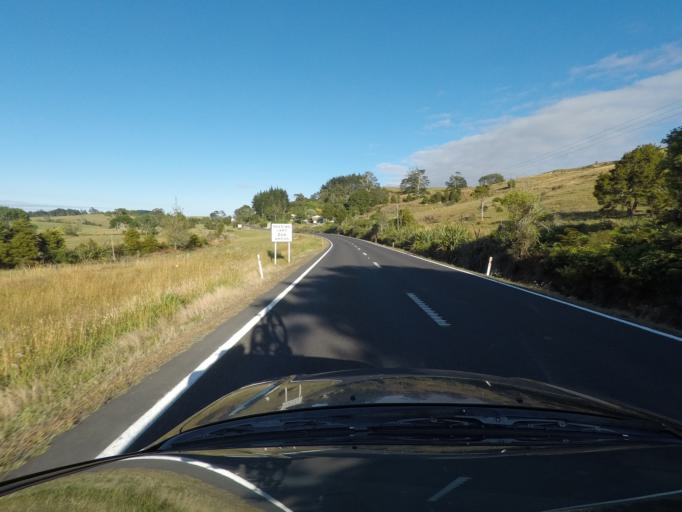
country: NZ
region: Northland
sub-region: Far North District
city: Kawakawa
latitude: -35.4954
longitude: 174.1445
